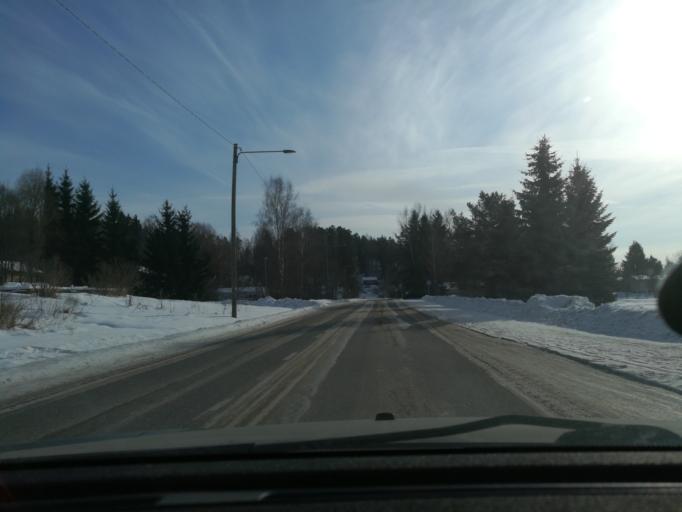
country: FI
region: Uusimaa
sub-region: Helsinki
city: Saukkola
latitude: 60.4715
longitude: 23.9878
